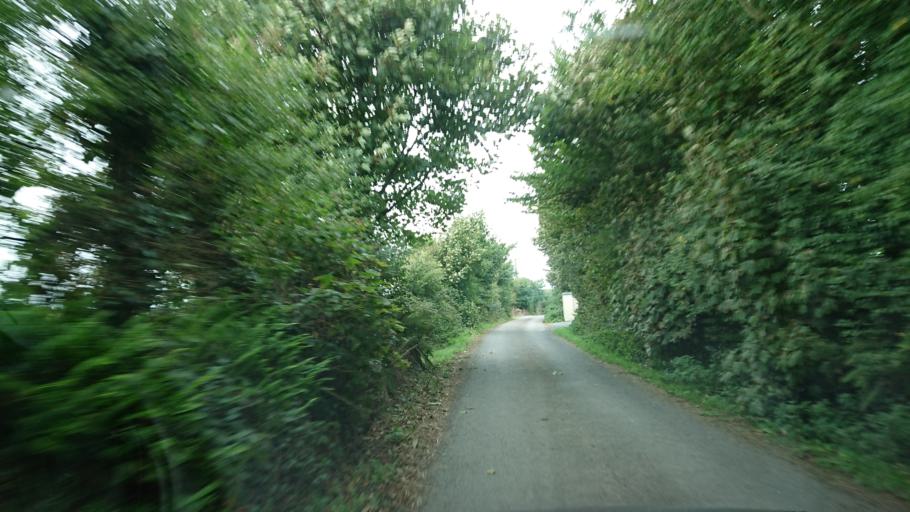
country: IE
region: Munster
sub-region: Waterford
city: Waterford
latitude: 52.2141
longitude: -7.0426
